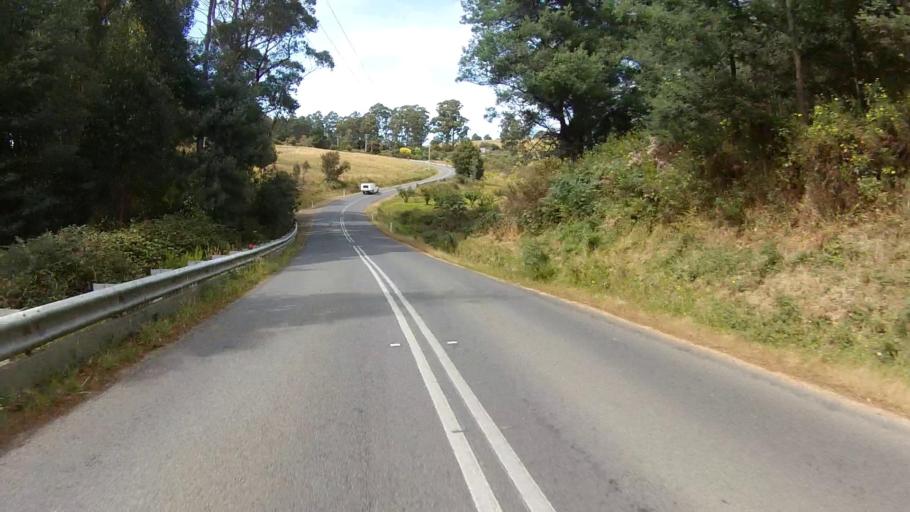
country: AU
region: Tasmania
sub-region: Kingborough
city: Kettering
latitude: -43.1974
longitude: 147.2507
